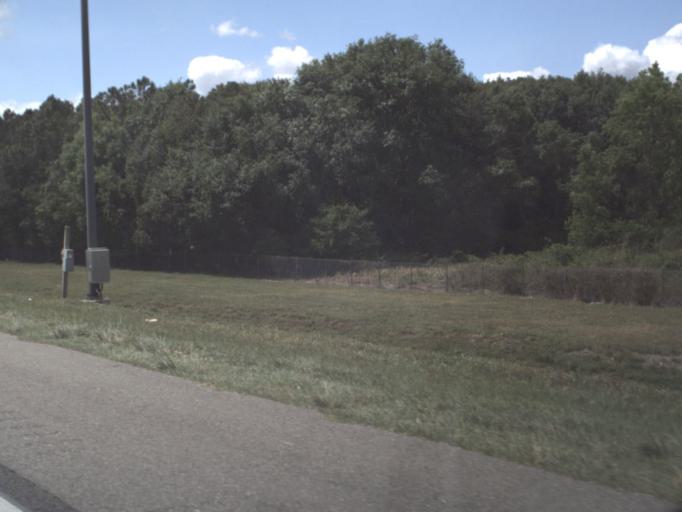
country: US
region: Florida
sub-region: Orange County
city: Ocoee
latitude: 28.5840
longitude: -81.5575
